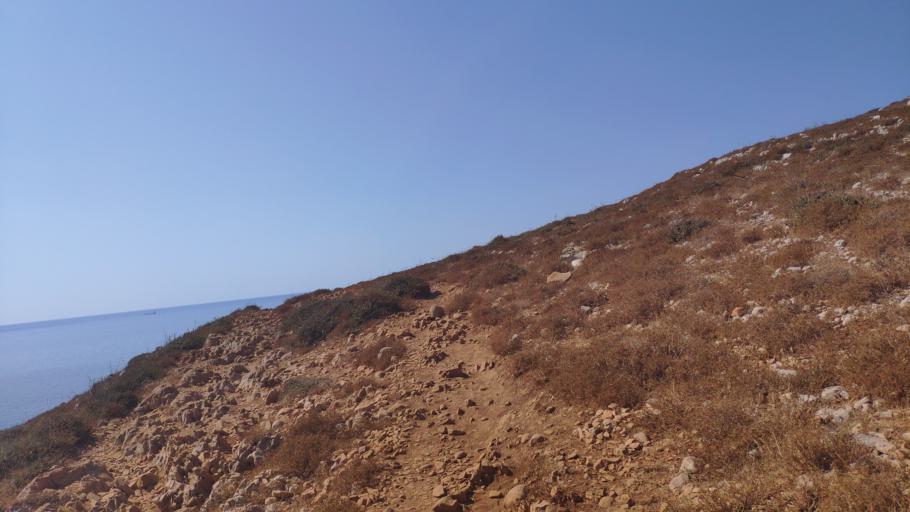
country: GR
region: Peloponnese
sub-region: Nomos Lakonias
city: Gytheio
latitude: 36.3923
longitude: 22.4837
